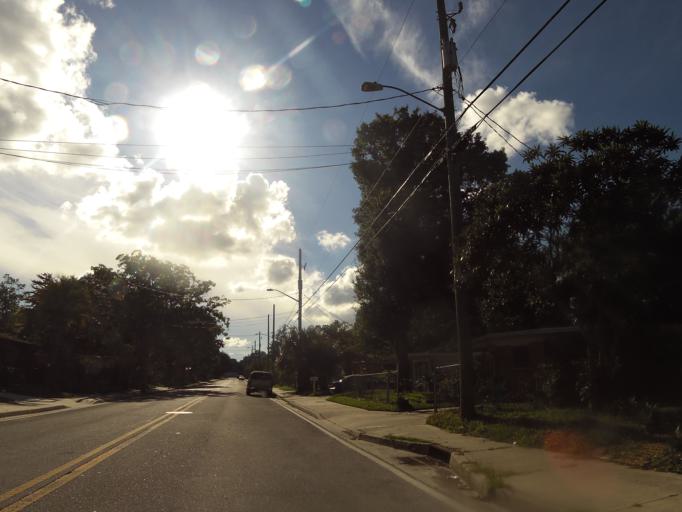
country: US
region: Florida
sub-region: Duval County
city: Jacksonville
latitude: 30.3513
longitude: -81.6976
